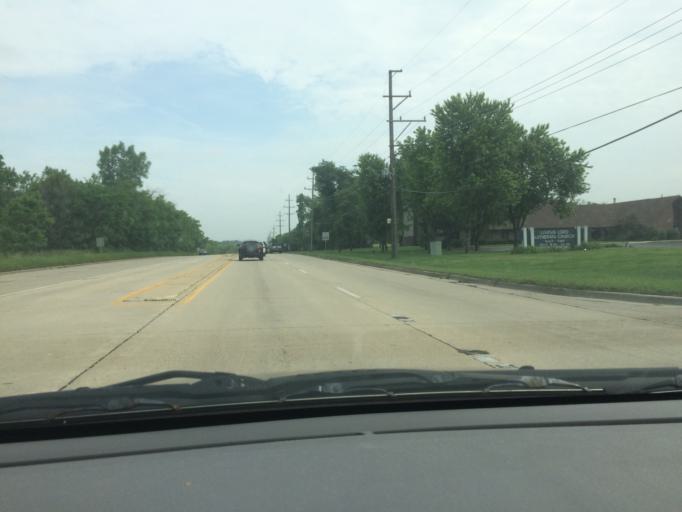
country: US
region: Illinois
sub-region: Cook County
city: Bartlett
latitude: 41.9677
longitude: -88.2066
